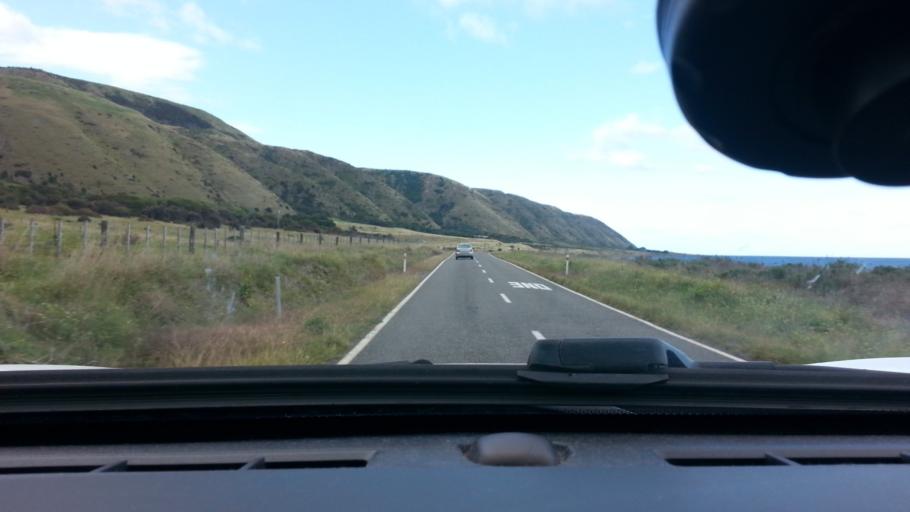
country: NZ
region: Wellington
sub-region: South Wairarapa District
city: Waipawa
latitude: -41.4967
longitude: 175.2093
